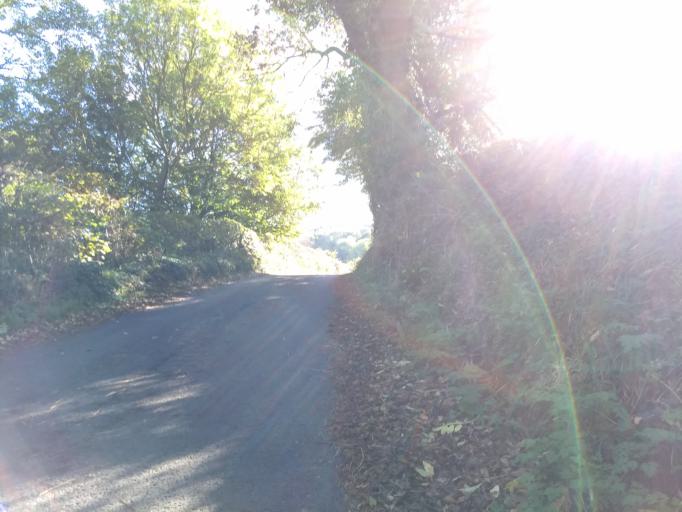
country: GB
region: England
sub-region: Isle of Wight
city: Ventnor
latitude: 50.6025
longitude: -1.2286
